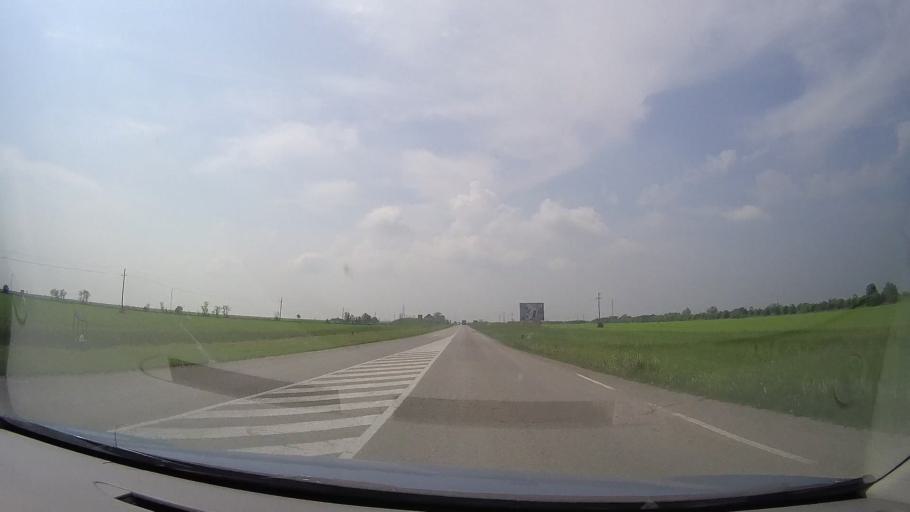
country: RS
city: Debeljaca
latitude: 45.0755
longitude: 20.6409
